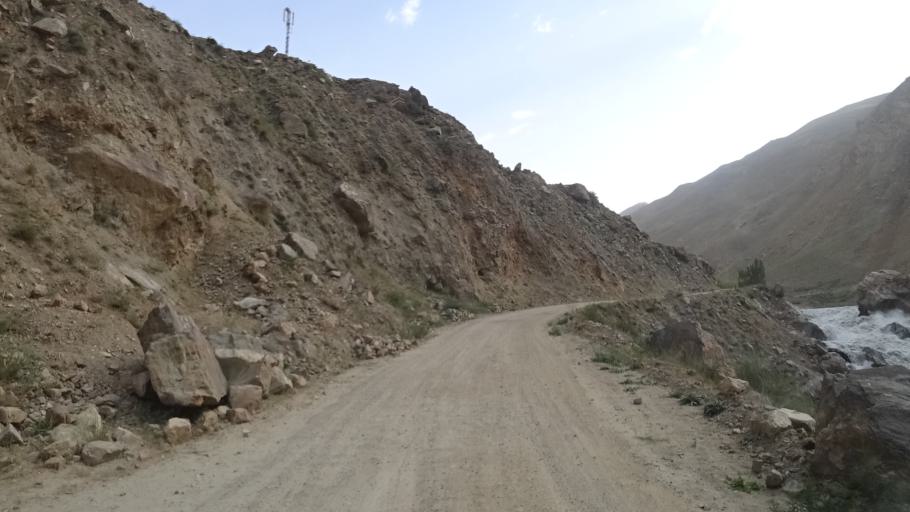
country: TJ
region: Gorno-Badakhshan
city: Khorugh
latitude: 37.2616
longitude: 71.4873
